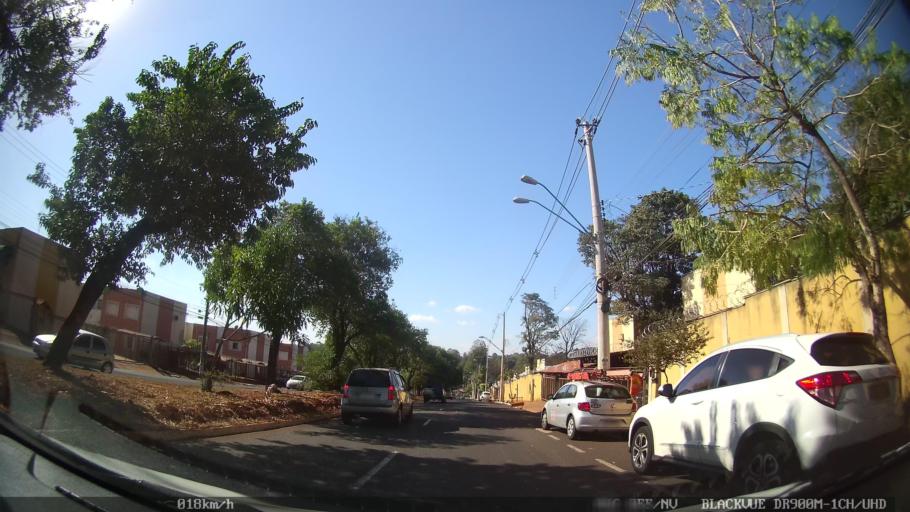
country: BR
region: Sao Paulo
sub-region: Ribeirao Preto
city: Ribeirao Preto
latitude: -21.1695
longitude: -47.7912
